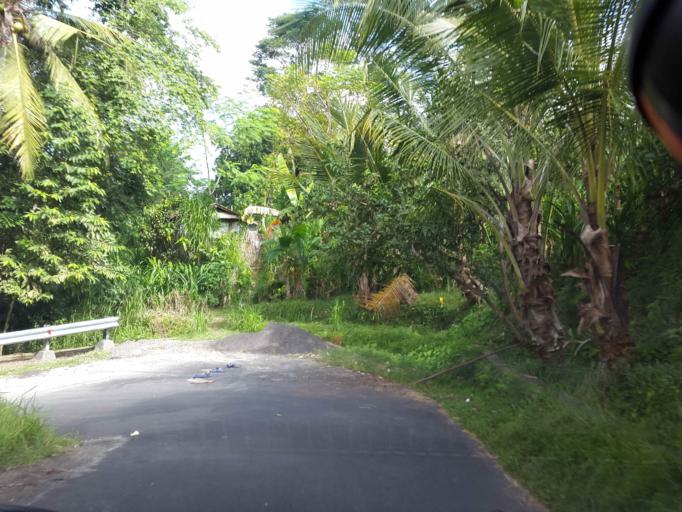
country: ID
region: Bali
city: Banjar Kelodan
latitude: -8.5188
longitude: 115.3692
